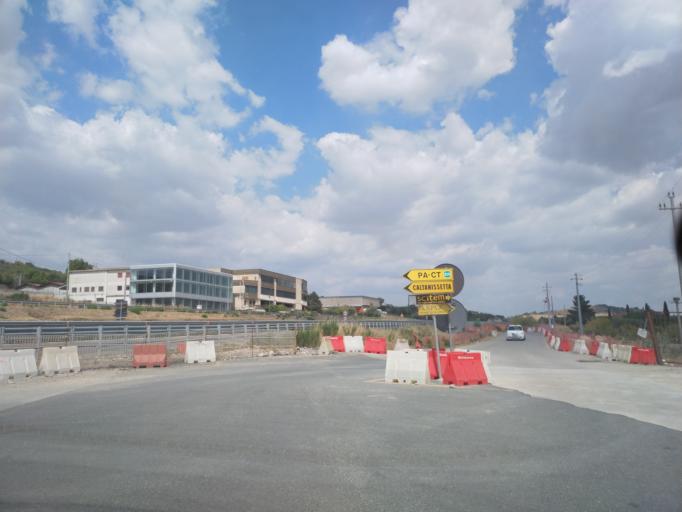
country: IT
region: Sicily
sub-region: Provincia di Caltanissetta
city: San Cataldo
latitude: 37.4524
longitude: 13.9781
